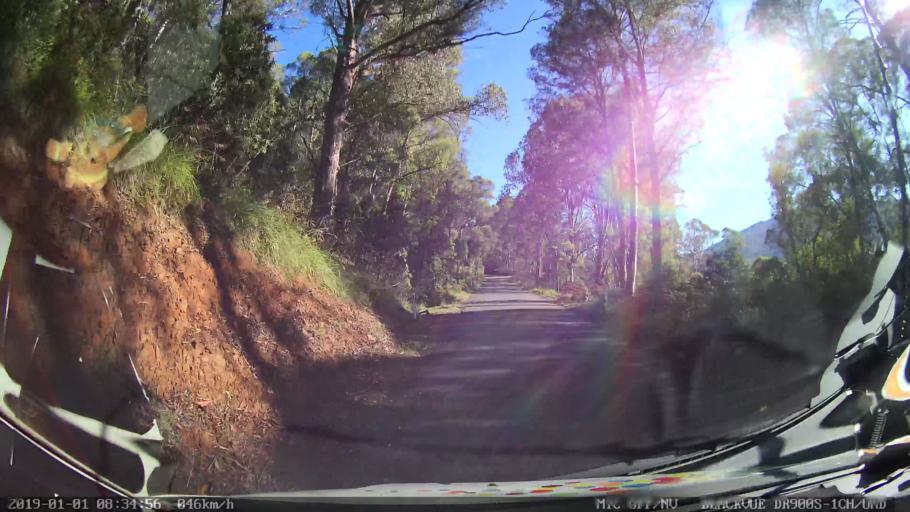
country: AU
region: New South Wales
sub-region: Snowy River
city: Jindabyne
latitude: -36.3522
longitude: 148.1928
